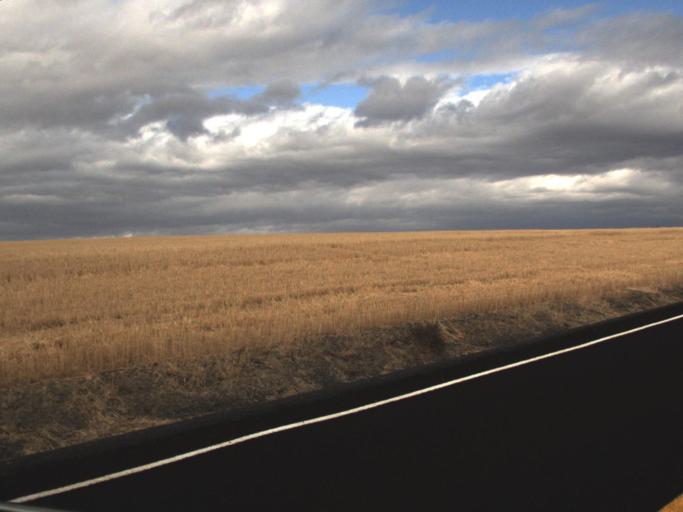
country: US
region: Washington
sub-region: Okanogan County
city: Coulee Dam
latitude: 47.8213
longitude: -118.7218
